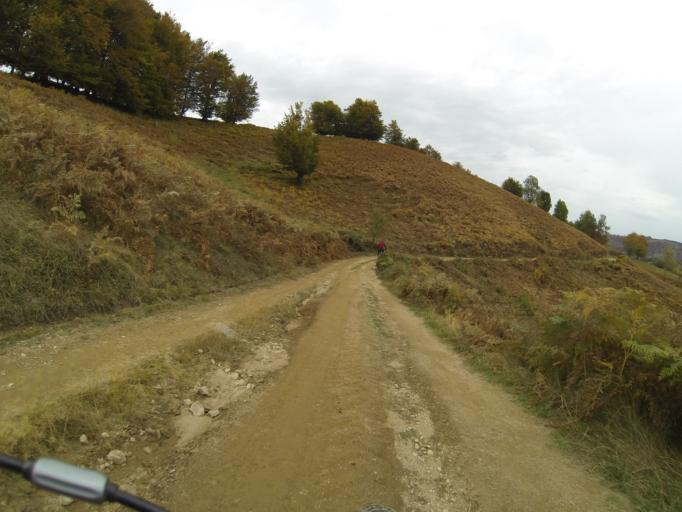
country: RO
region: Gorj
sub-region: Comuna Pades
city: Closani
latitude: 45.1153
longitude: 22.8492
